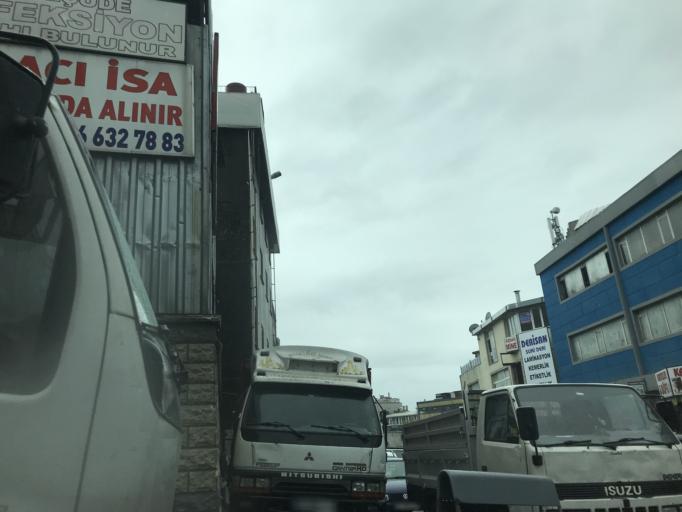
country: TR
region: Istanbul
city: merter keresteciler
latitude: 41.0206
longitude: 28.8835
